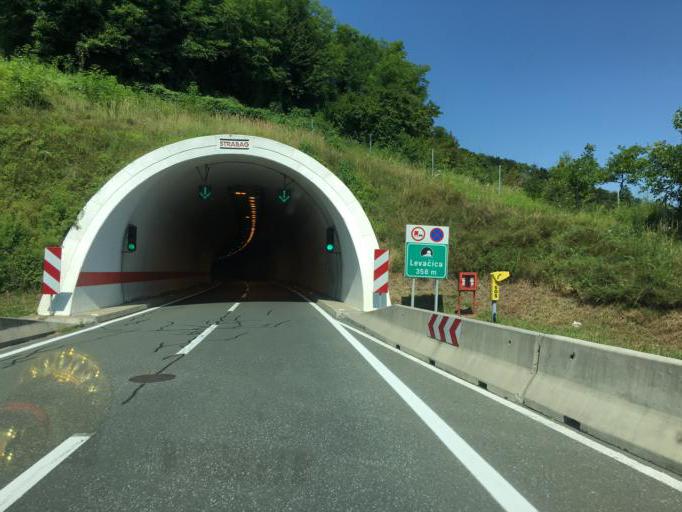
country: HR
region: Krapinsko-Zagorska
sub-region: Grad Krapina
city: Krapina
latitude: 46.1367
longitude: 15.8687
